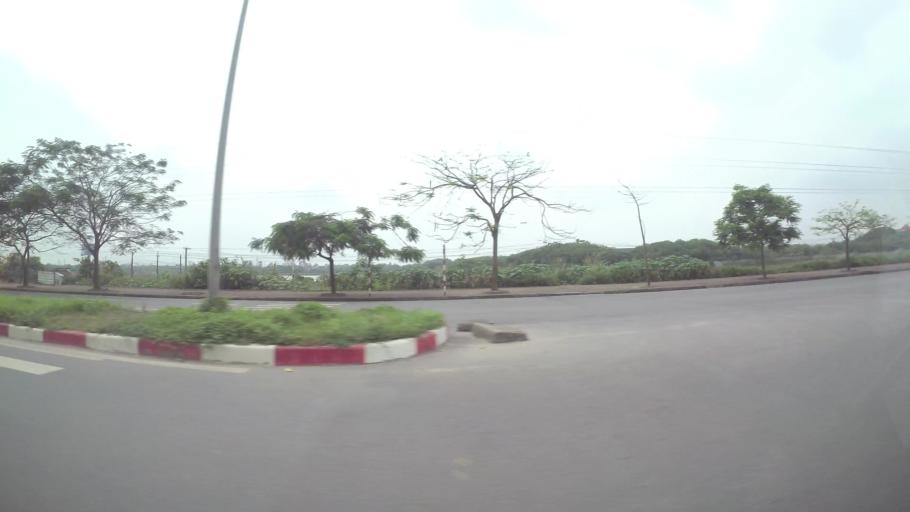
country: VN
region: Ha Noi
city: Trau Quy
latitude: 21.0324
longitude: 105.9288
